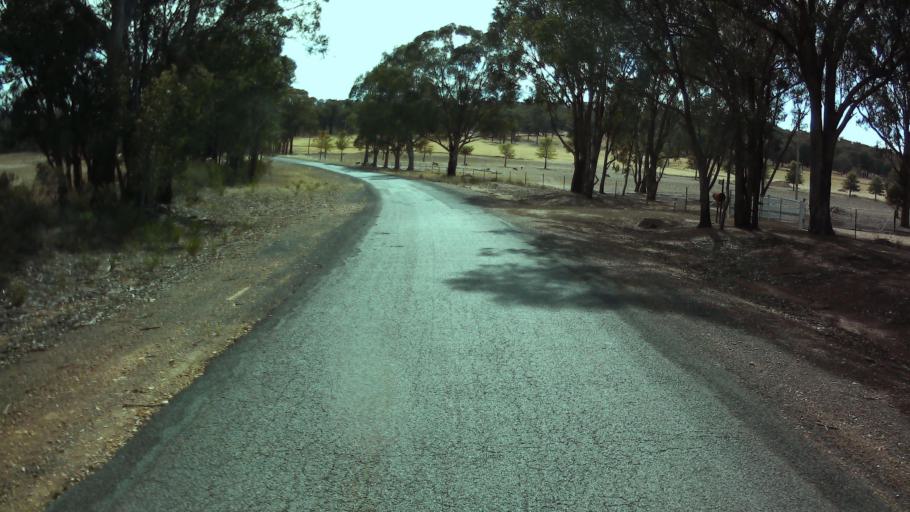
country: AU
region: New South Wales
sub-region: Weddin
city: Grenfell
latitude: -33.8492
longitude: 148.2308
